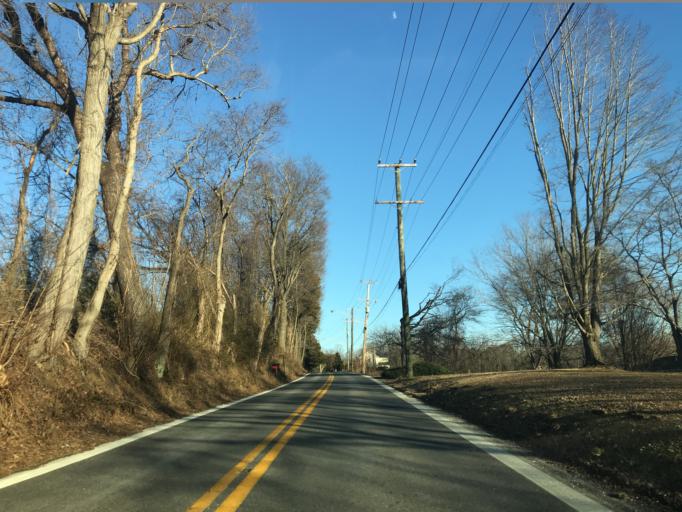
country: US
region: Maryland
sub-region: Prince George's County
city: Marlboro Meadows
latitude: 38.8435
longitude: -76.6605
